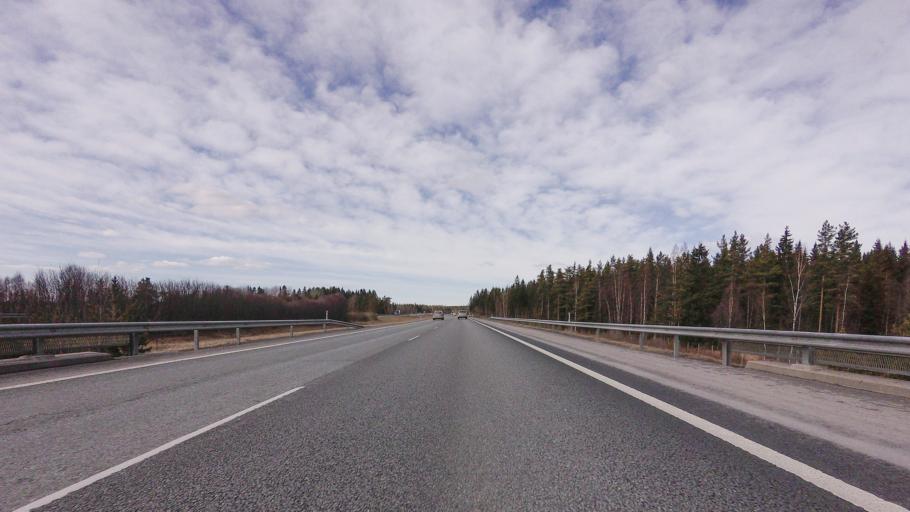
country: FI
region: Pirkanmaa
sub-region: Etelae-Pirkanmaa
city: Viiala
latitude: 61.2684
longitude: 23.8232
